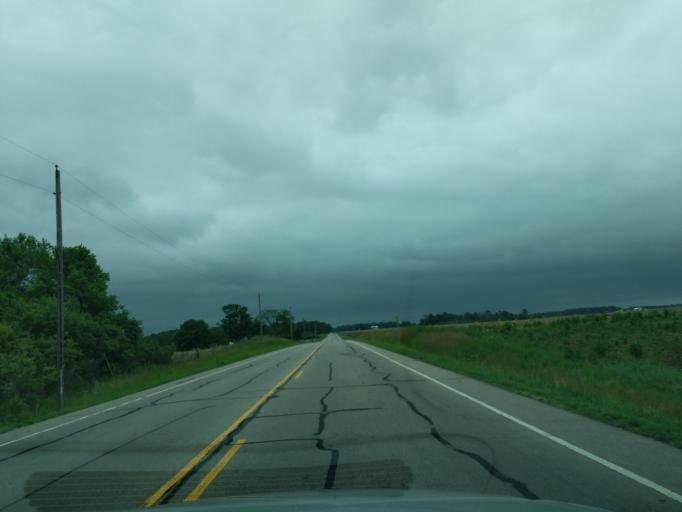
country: US
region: Indiana
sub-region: Madison County
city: Alexandria
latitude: 40.2774
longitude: -85.6315
